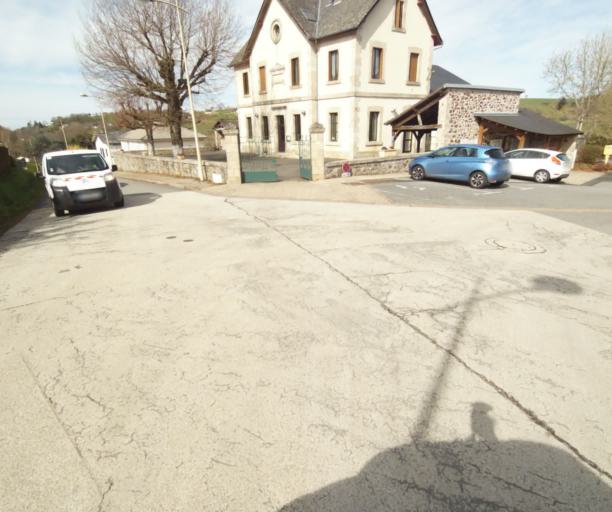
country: FR
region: Limousin
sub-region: Departement de la Correze
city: Laguenne
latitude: 45.2638
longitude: 1.8191
